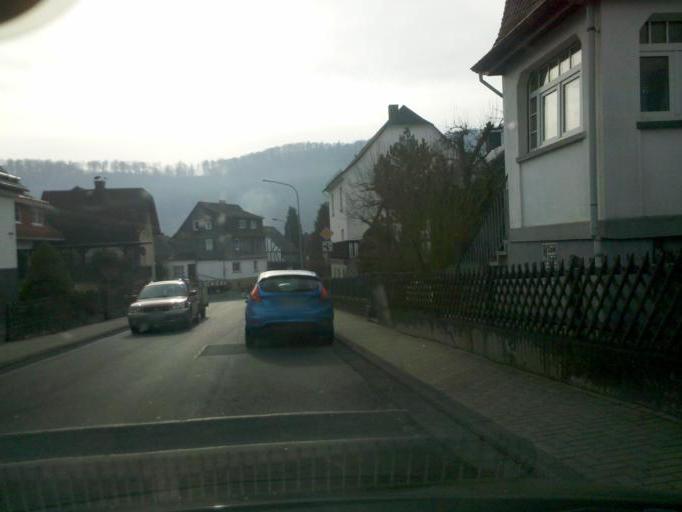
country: DE
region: Hesse
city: Dillenburg
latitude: 50.7749
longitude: 8.2973
